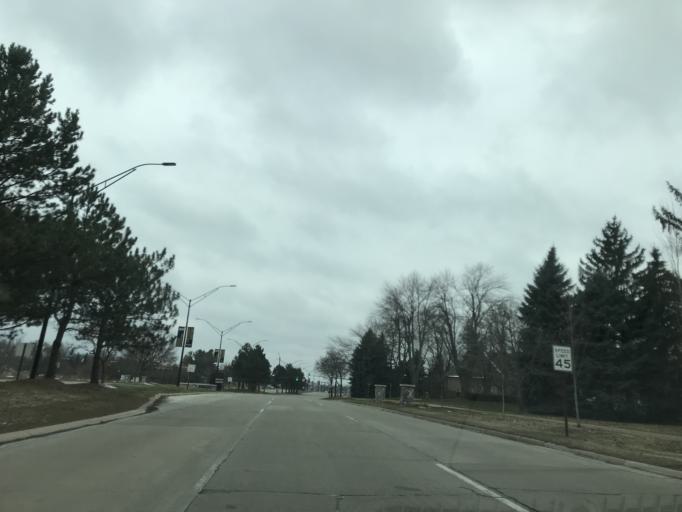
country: US
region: Michigan
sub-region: Oakland County
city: Auburn Hills
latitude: 42.6718
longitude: -83.2285
